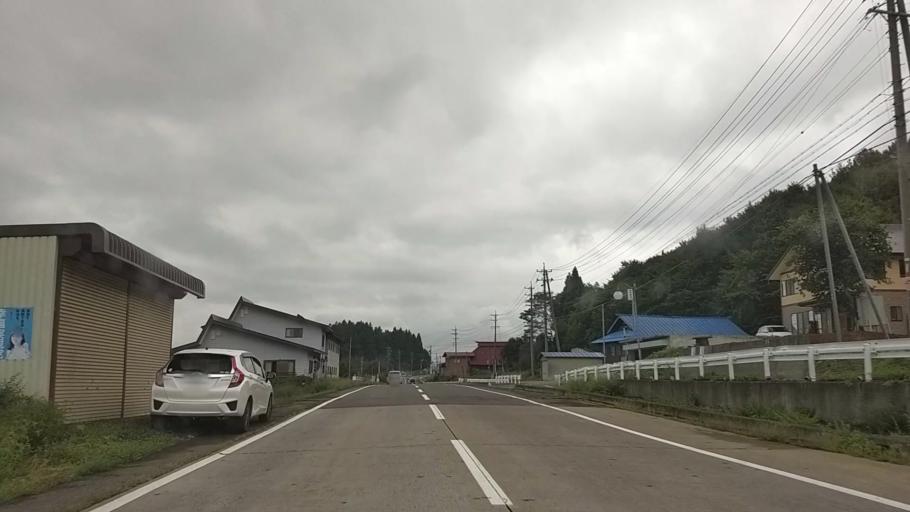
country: JP
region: Nagano
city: Iiyama
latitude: 36.8047
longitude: 138.3288
